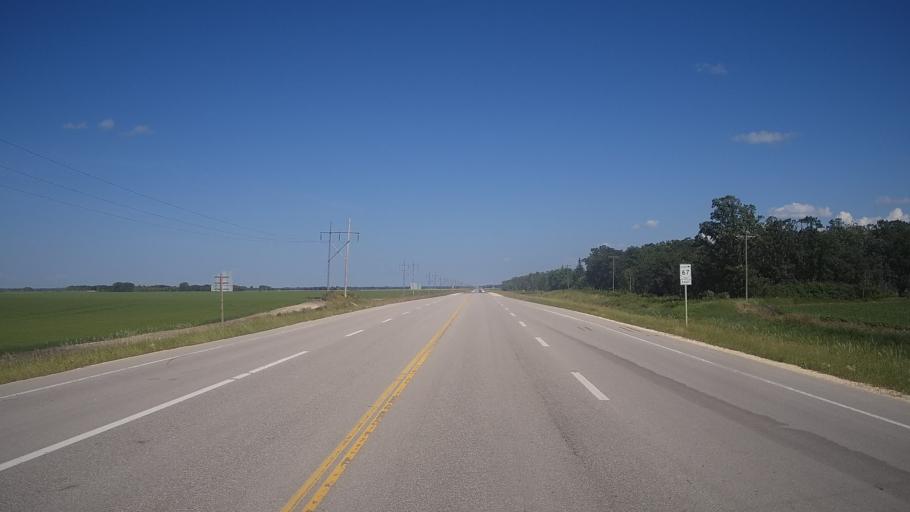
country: CA
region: Manitoba
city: Stonewall
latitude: 50.1227
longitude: -97.4364
